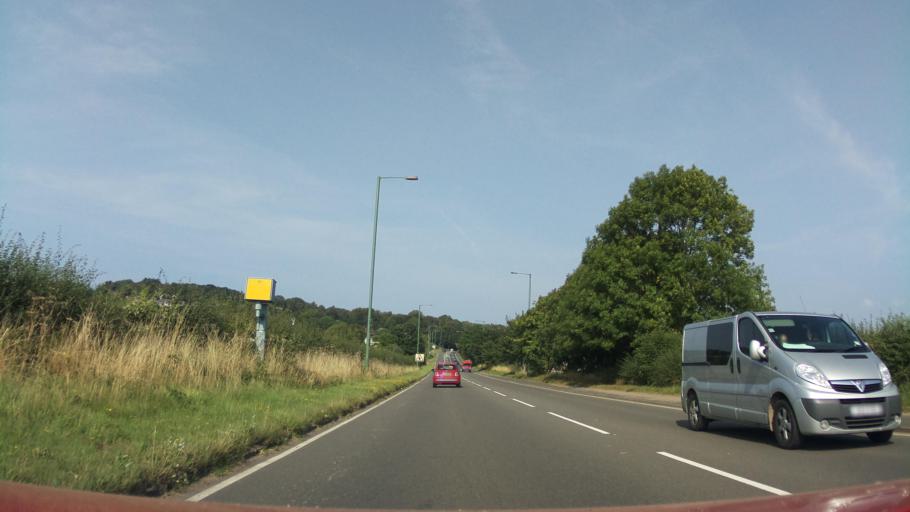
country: GB
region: England
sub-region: Walsall
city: Aldridge
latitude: 52.6253
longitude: -1.8991
